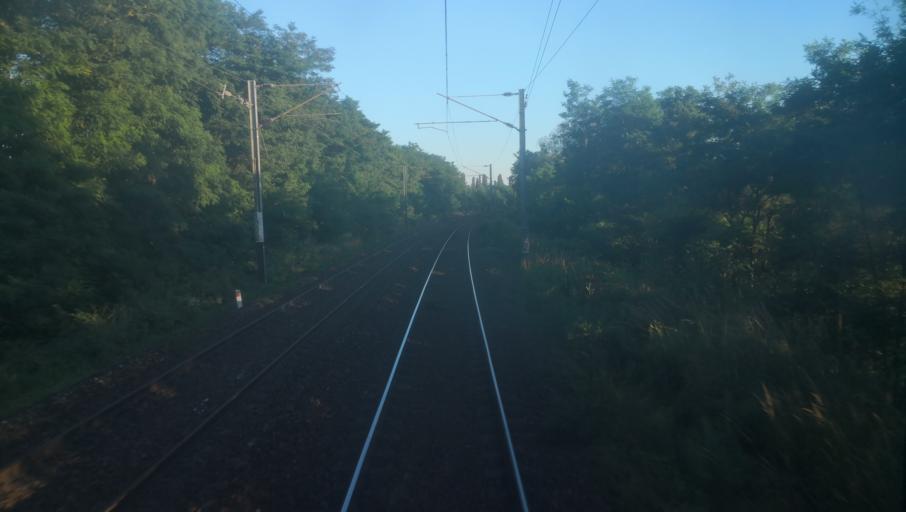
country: FR
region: Bourgogne
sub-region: Departement de la Nievre
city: Nevers
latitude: 46.9747
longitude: 3.1549
